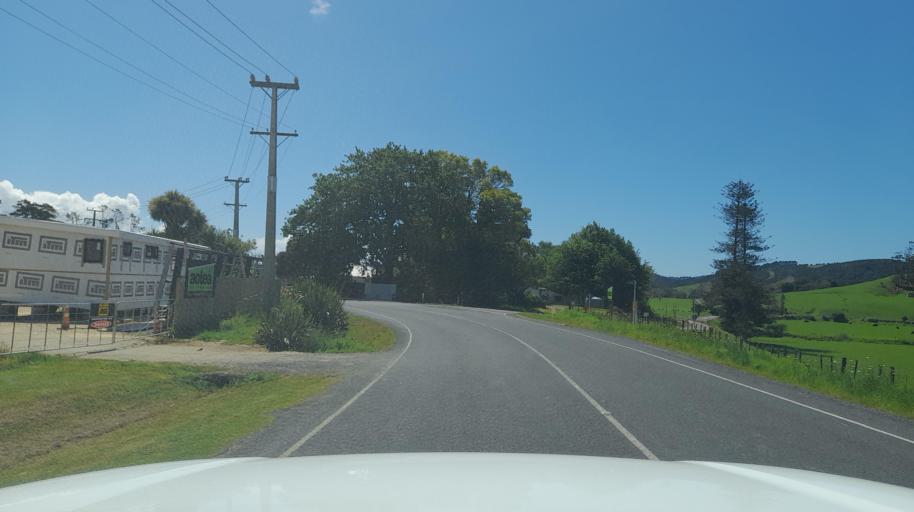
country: NZ
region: Northland
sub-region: Far North District
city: Taipa
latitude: -35.0434
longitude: 173.4966
